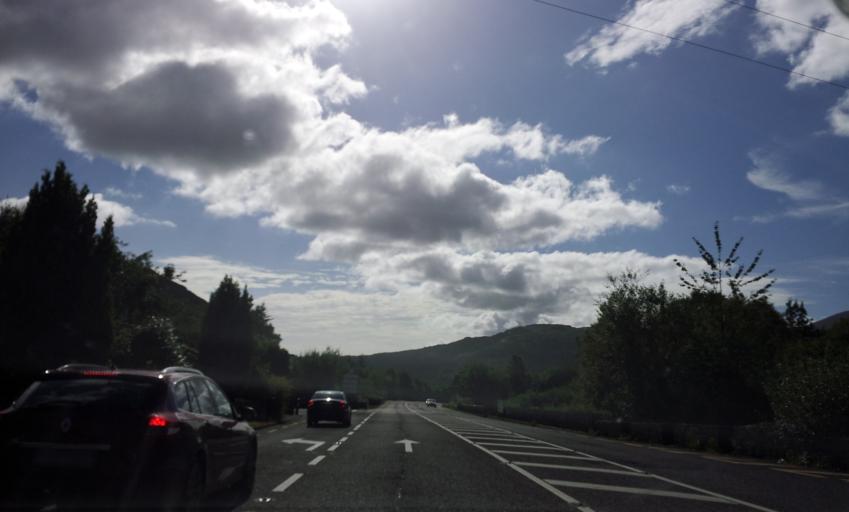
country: IE
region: Munster
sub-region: Ciarrai
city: Cill Airne
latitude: 51.9824
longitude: -9.3127
